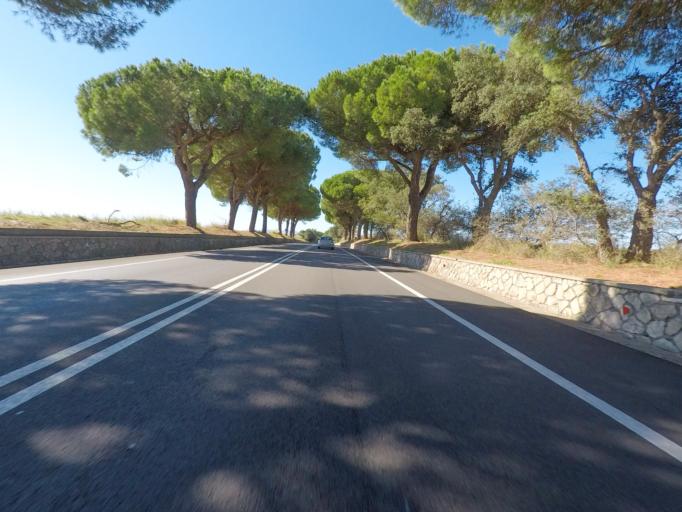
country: IT
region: Latium
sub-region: Provincia di Viterbo
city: Pescia Romana
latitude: 42.4143
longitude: 11.4567
